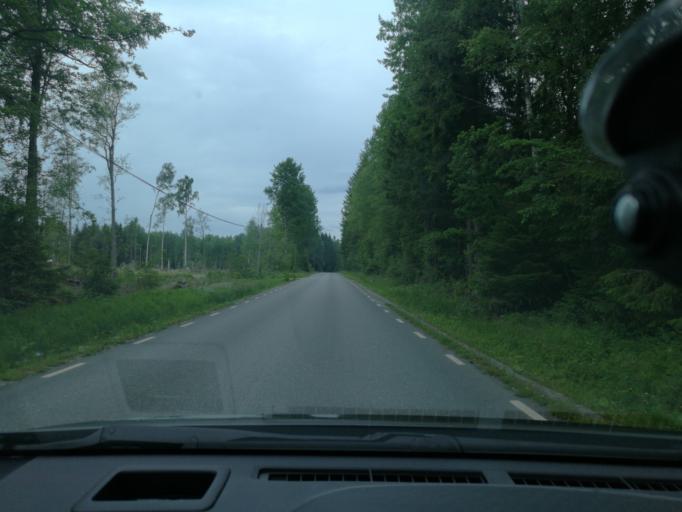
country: SE
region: Vaestmanland
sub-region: Vasteras
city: Skultuna
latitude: 59.7839
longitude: 16.3742
